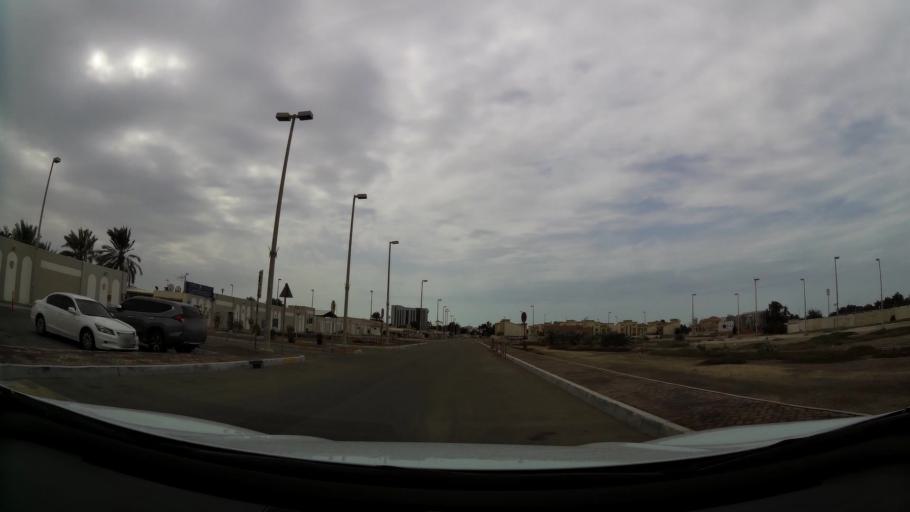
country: AE
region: Abu Dhabi
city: Abu Dhabi
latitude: 24.4326
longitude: 54.4253
